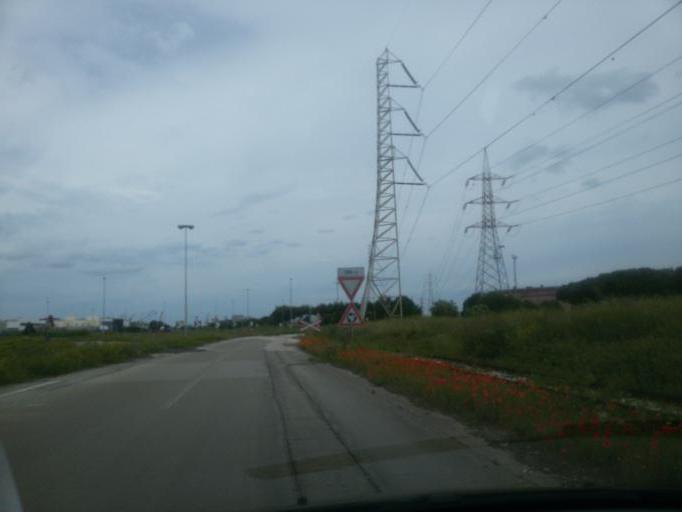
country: IT
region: Apulia
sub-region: Provincia di Brindisi
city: Materdomini
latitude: 40.6363
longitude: 17.9769
